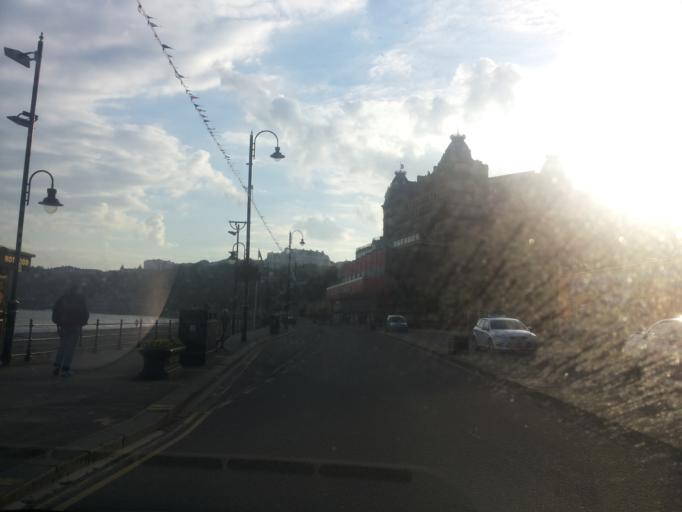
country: GB
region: England
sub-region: North Yorkshire
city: Scarborough
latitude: 54.2822
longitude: -0.3960
